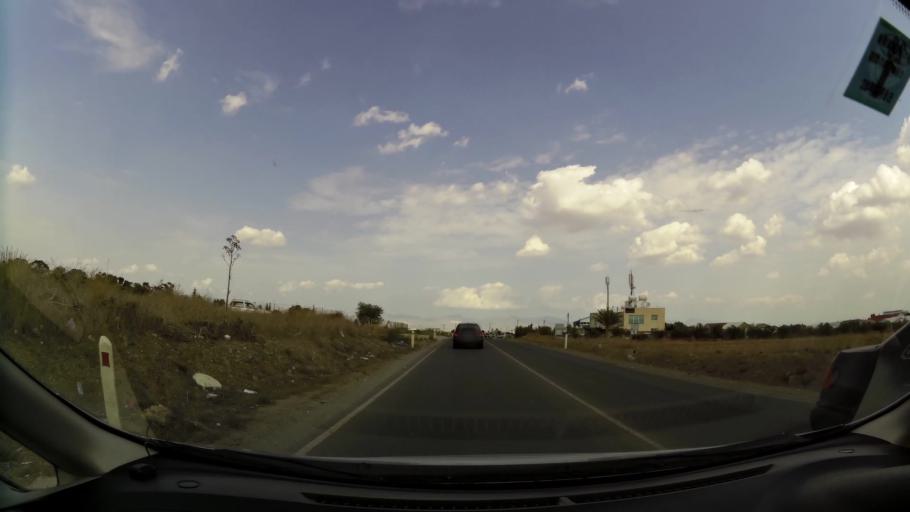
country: CY
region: Lefkosia
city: Tseri
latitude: 35.1004
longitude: 33.3276
